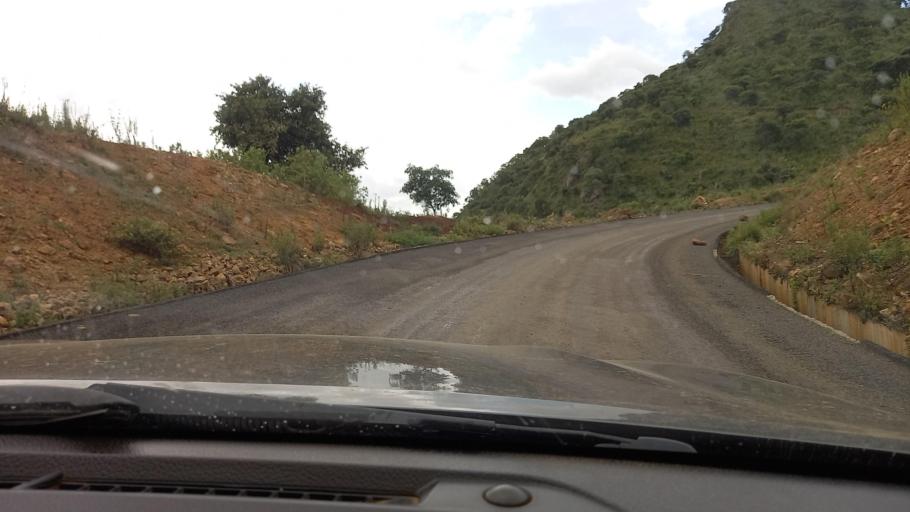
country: ET
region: Southern Nations, Nationalities, and People's Region
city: Mizan Teferi
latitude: 6.2025
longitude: 35.6523
